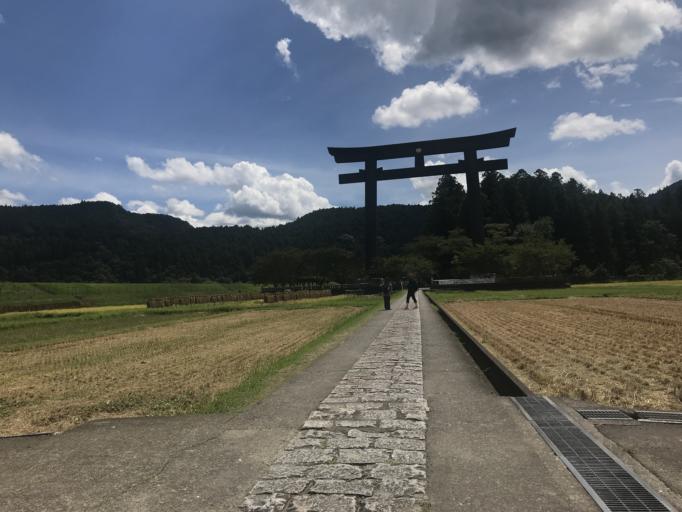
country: JP
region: Wakayama
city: Shingu
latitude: 33.8370
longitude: 135.7756
